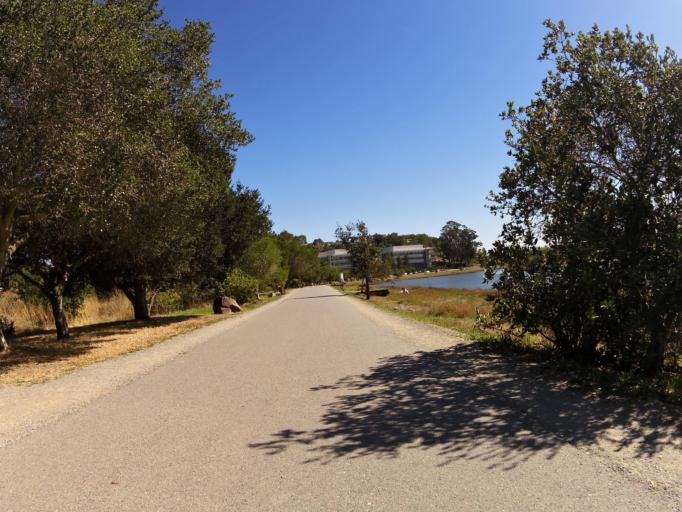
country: US
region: California
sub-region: Marin County
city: Larkspur
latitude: 37.9481
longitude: -122.5416
